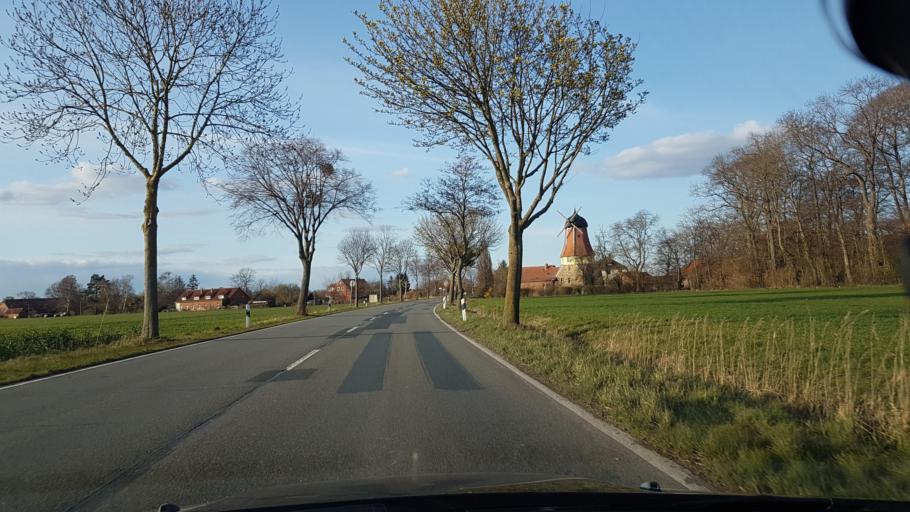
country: DE
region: Lower Saxony
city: Grossgoltern
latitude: 52.3528
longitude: 9.5476
